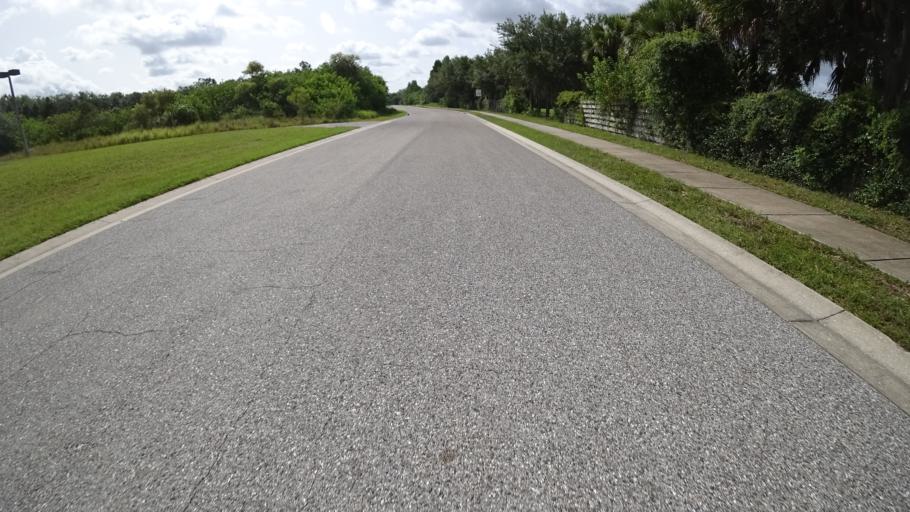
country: US
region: Florida
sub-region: Sarasota County
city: Desoto Lakes
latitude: 27.4402
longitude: -82.4667
